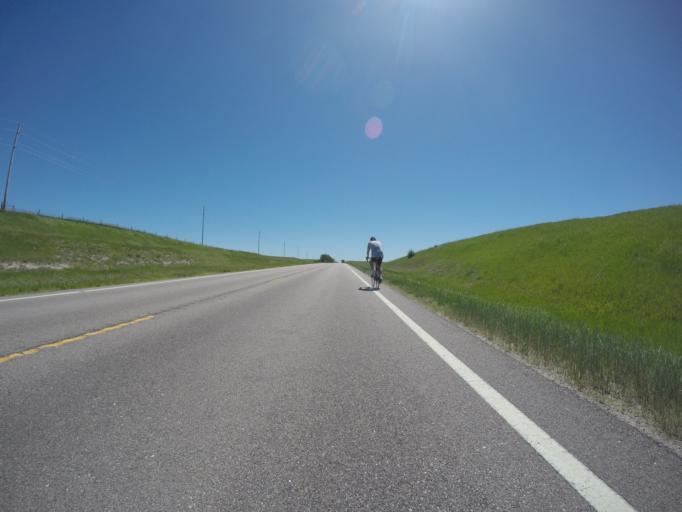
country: US
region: Kansas
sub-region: Norton County
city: Norton
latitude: 39.8283
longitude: -99.7024
